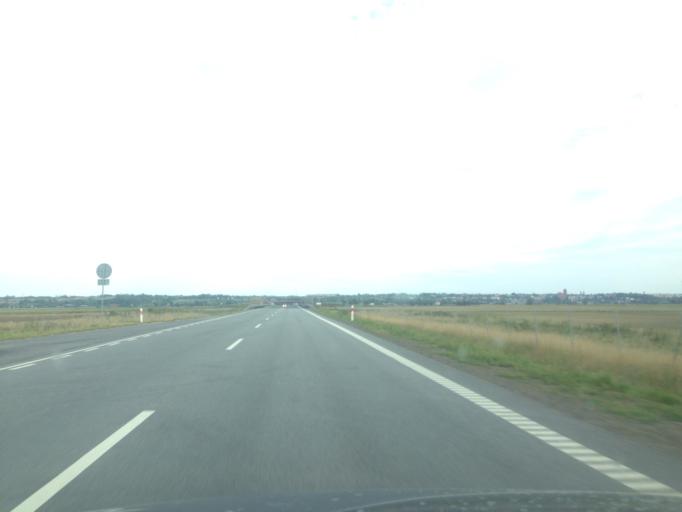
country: PL
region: Pomeranian Voivodeship
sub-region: Powiat kwidzynski
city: Kwidzyn
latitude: 53.7580
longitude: 18.8853
